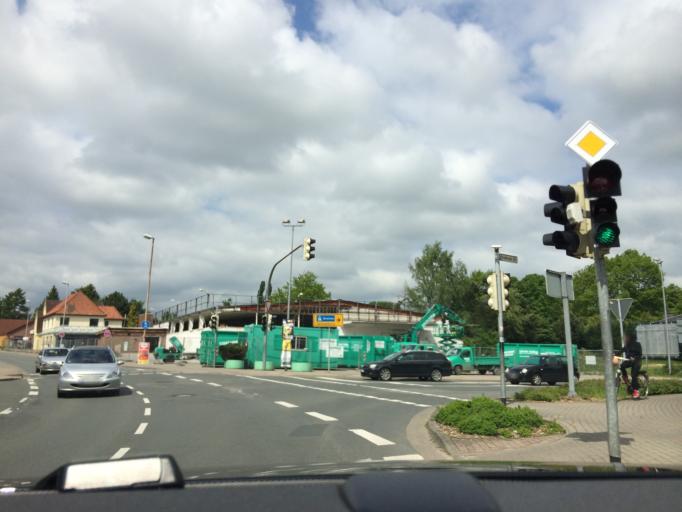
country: DE
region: Lower Saxony
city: Ganderkesee
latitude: 53.0339
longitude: 8.5476
